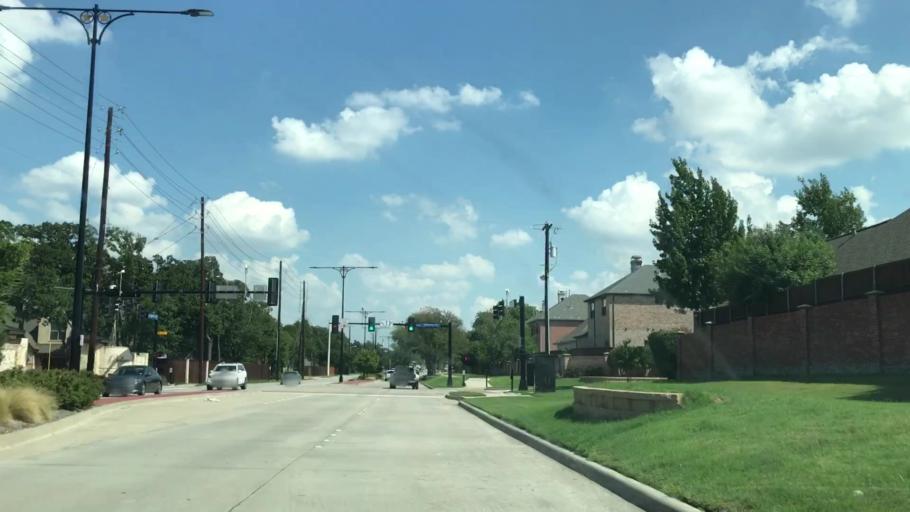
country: US
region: Texas
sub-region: Dallas County
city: Coppell
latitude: 32.9696
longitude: -97.0012
